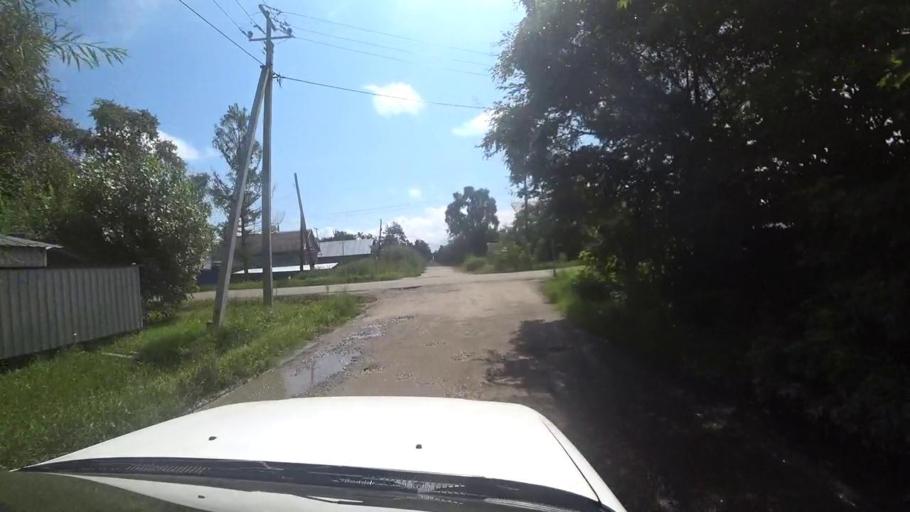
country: RU
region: Primorskiy
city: Dal'nerechensk
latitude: 45.9304
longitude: 133.7395
